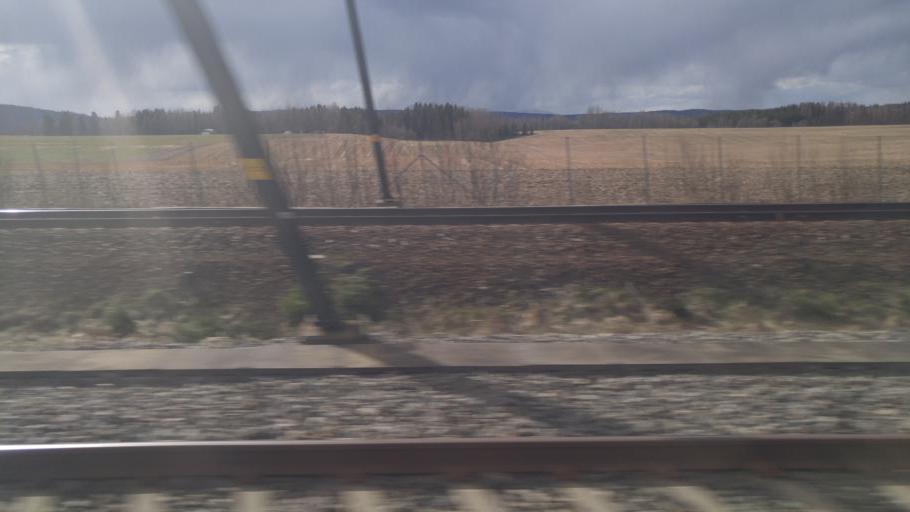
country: NO
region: Akershus
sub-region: Ullensaker
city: Klofta
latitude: 60.0589
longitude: 11.1399
